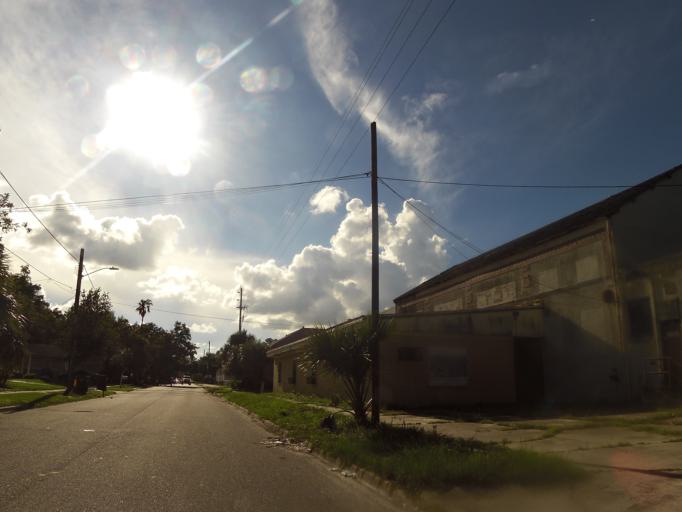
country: US
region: Florida
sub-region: Duval County
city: Jacksonville
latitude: 30.3535
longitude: -81.6778
